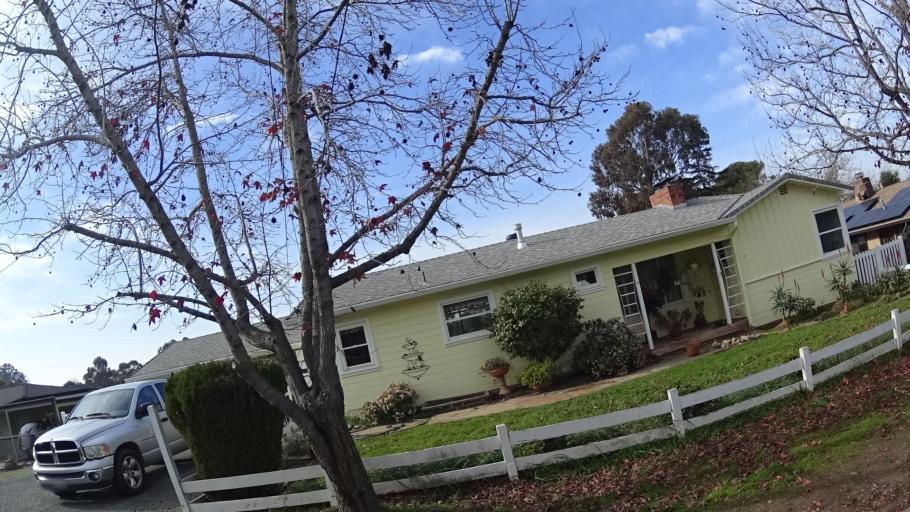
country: US
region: California
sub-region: Alameda County
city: Fairview
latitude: 37.6777
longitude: -122.0601
